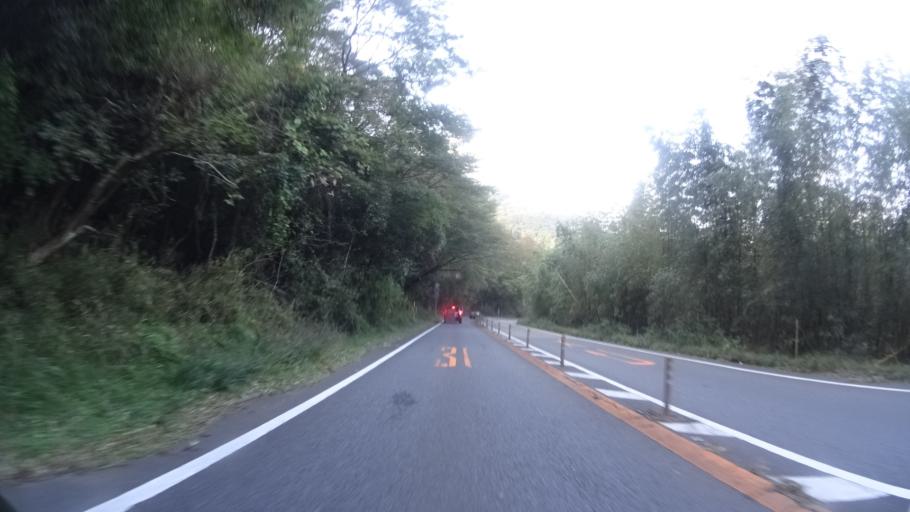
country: JP
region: Oita
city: Beppu
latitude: 33.2725
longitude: 131.4432
